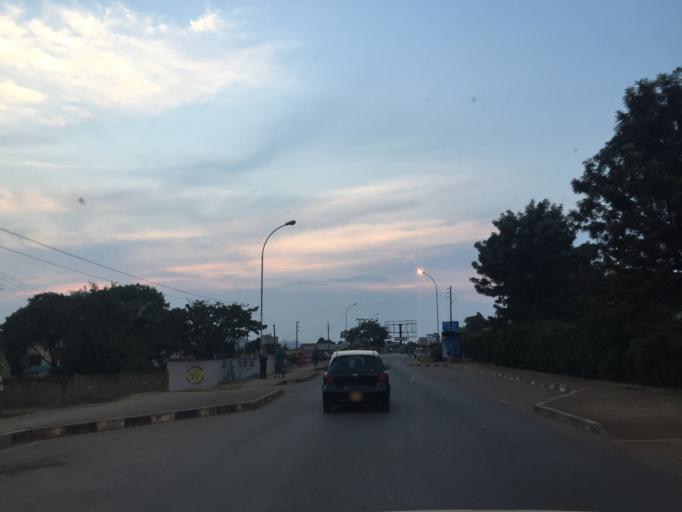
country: UG
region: Central Region
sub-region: Kampala District
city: Kampala
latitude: 0.2583
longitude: 32.6279
